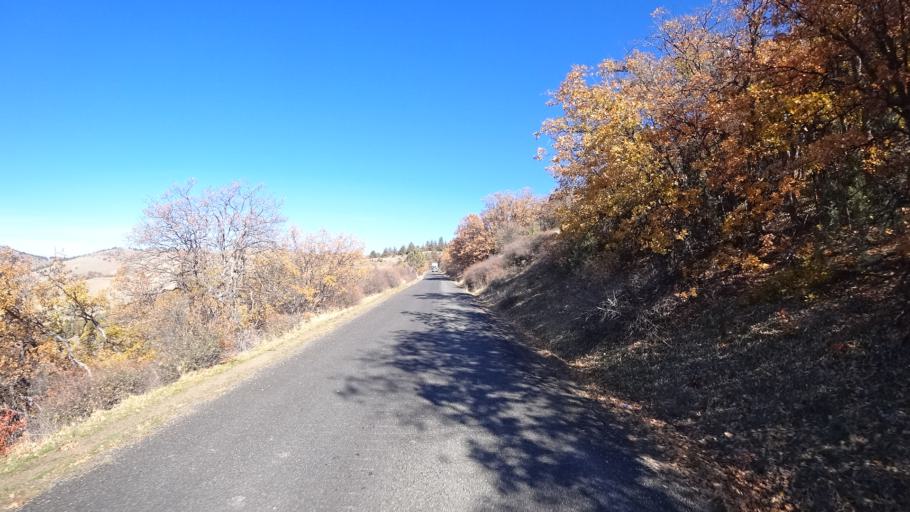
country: US
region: California
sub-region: Siskiyou County
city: Montague
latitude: 41.8274
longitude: -122.3343
